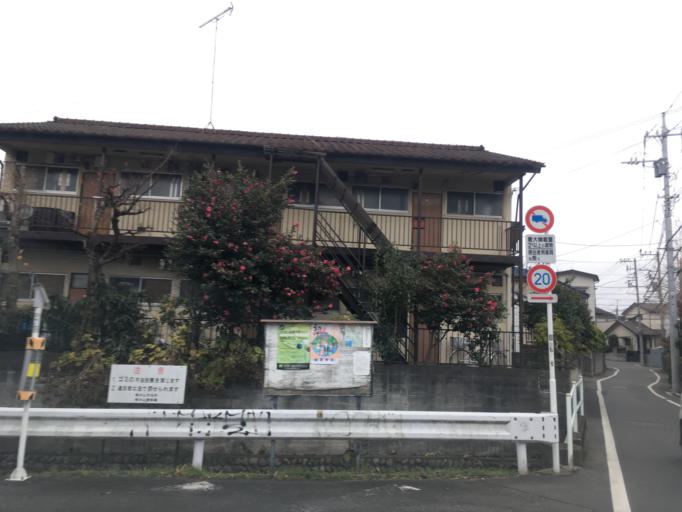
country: JP
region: Tokyo
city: Higashimurayama-shi
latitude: 35.7507
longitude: 139.4857
